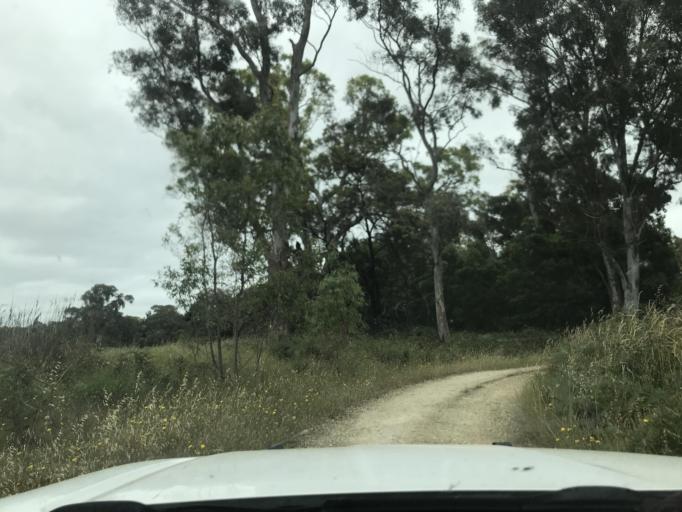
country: AU
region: South Australia
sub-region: Wattle Range
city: Penola
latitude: -37.1936
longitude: 140.9729
